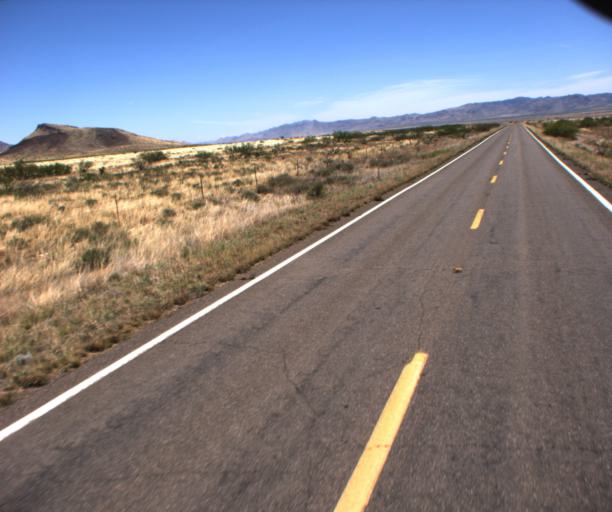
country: US
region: Arizona
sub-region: Cochise County
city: Douglas
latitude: 31.6389
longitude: -109.1810
